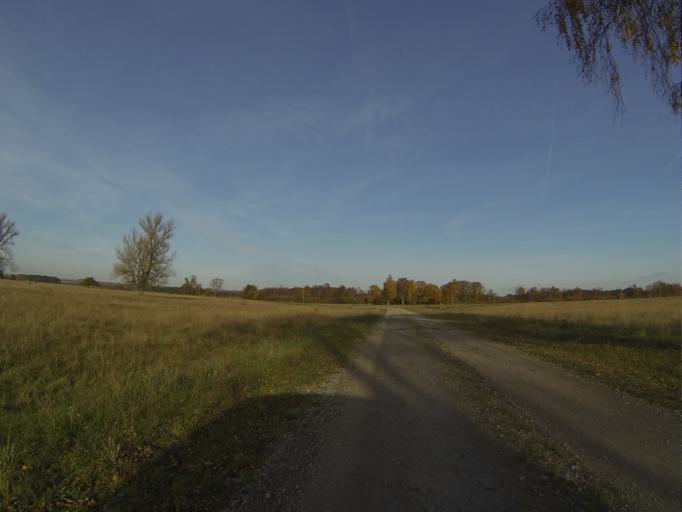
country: SE
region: Skane
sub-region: Lunds Kommun
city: Veberod
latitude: 55.7035
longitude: 13.4230
